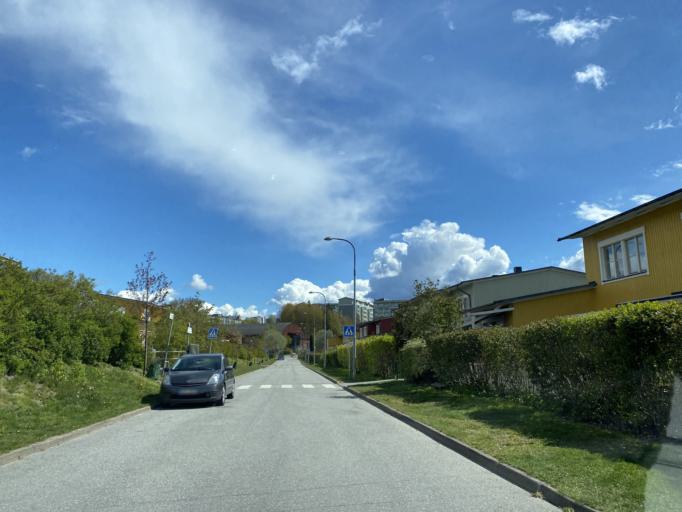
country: SE
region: Stockholm
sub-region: Stockholms Kommun
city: Kista
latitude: 59.4115
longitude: 17.9160
